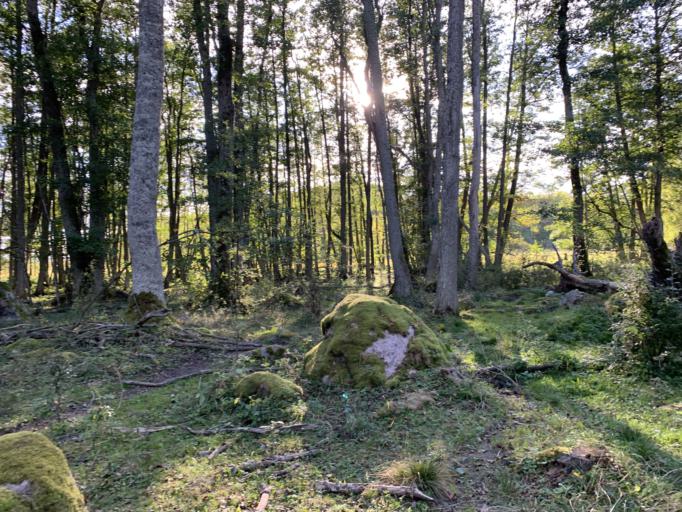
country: SE
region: Soedermanland
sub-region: Eskilstuna Kommun
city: Kvicksund
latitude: 59.4775
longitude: 16.2426
